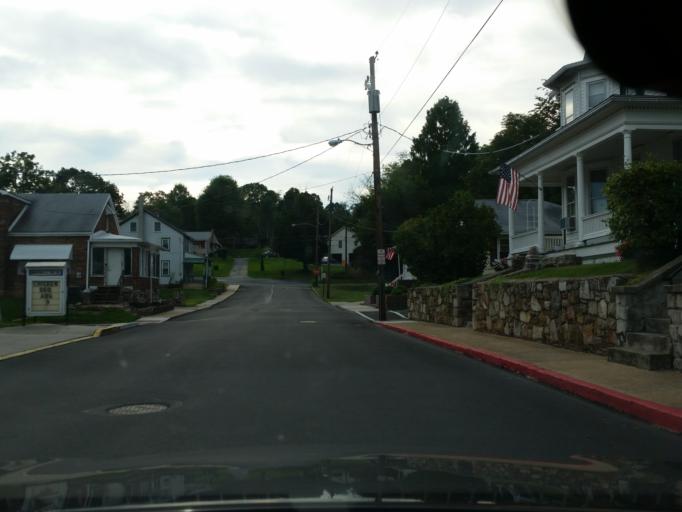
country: US
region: Pennsylvania
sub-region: Perry County
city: Marysville
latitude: 40.3414
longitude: -76.9323
